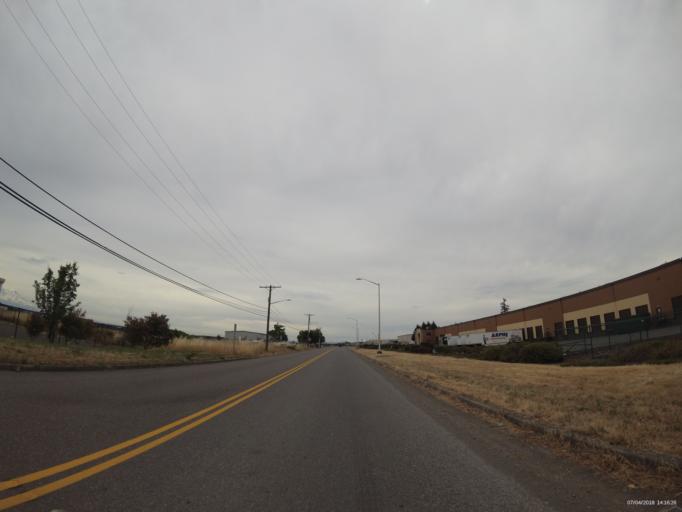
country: US
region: Washington
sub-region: Pierce County
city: McChord Air Force Base
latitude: 47.1576
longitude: -122.4807
